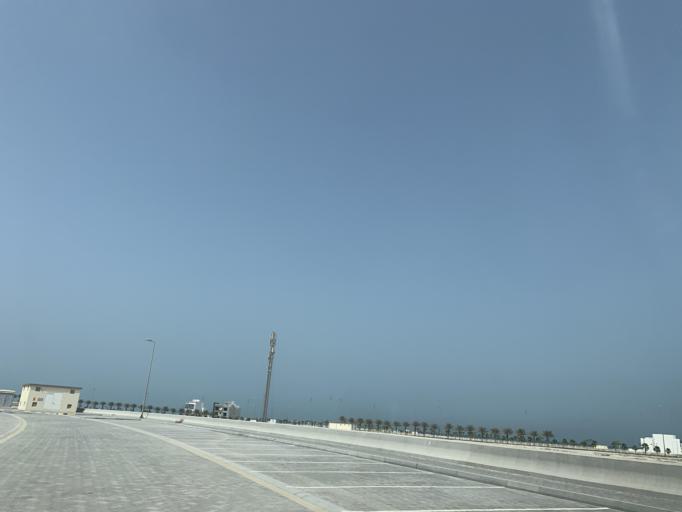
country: BH
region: Muharraq
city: Al Hadd
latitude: 26.2712
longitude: 50.6756
